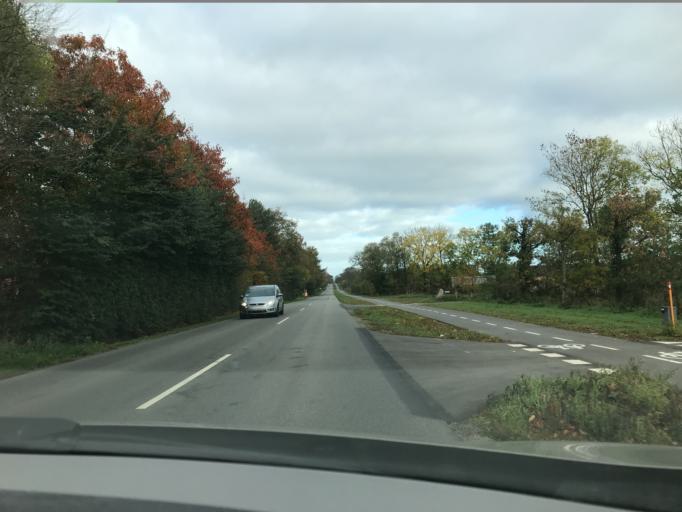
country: DK
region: South Denmark
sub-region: Kolding Kommune
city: Kolding
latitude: 55.5472
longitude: 9.4138
